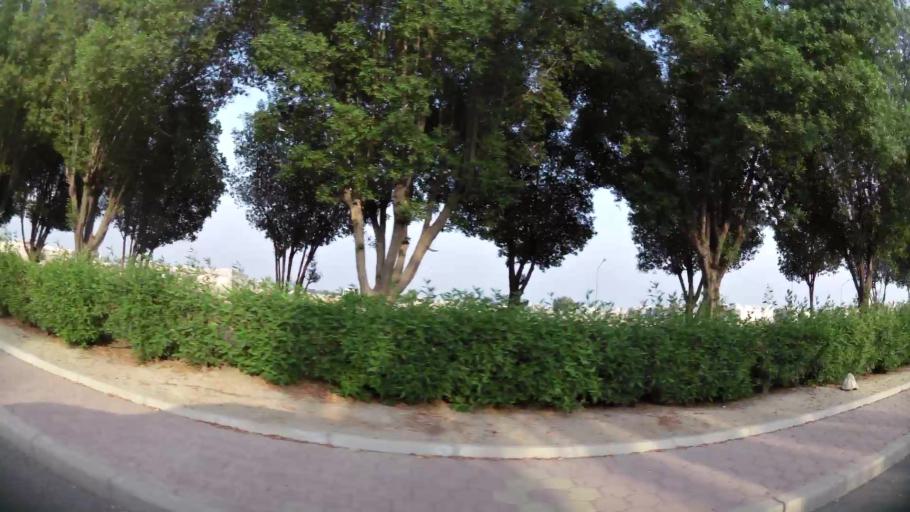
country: KW
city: Al Funaytis
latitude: 29.2394
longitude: 48.0835
